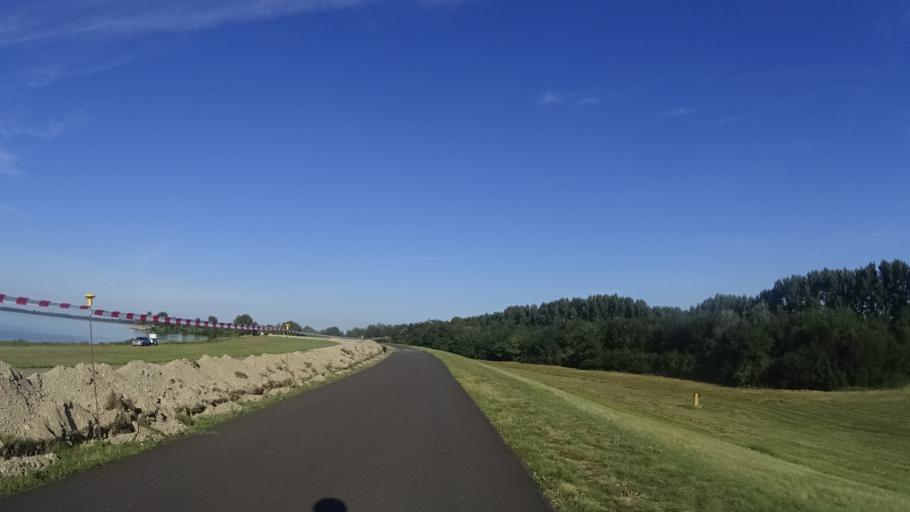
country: SK
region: Trnavsky
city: Samorin
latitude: 48.0202
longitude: 17.2868
